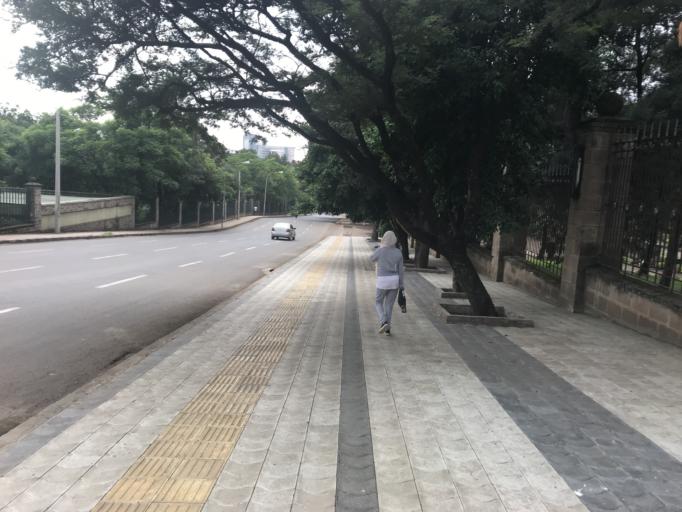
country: ET
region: Adis Abeba
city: Addis Ababa
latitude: 9.0169
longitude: 38.7628
